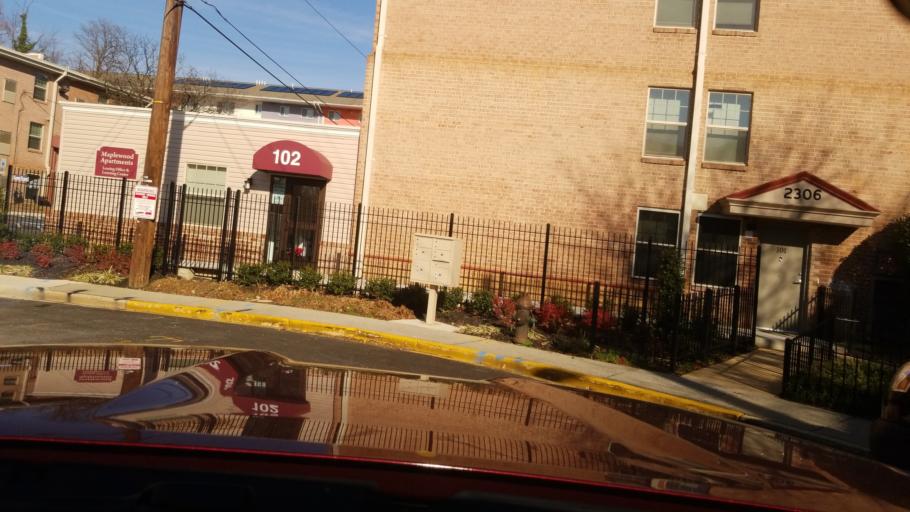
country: US
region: Maryland
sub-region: Prince George's County
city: Hillcrest Heights
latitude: 38.8548
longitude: -76.9725
